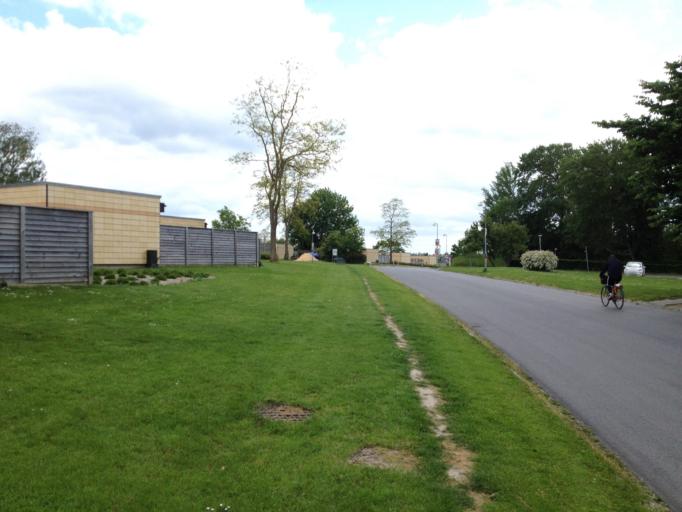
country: DK
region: Capital Region
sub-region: Fredensborg Kommune
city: Niva
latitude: 55.9380
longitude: 12.4878
